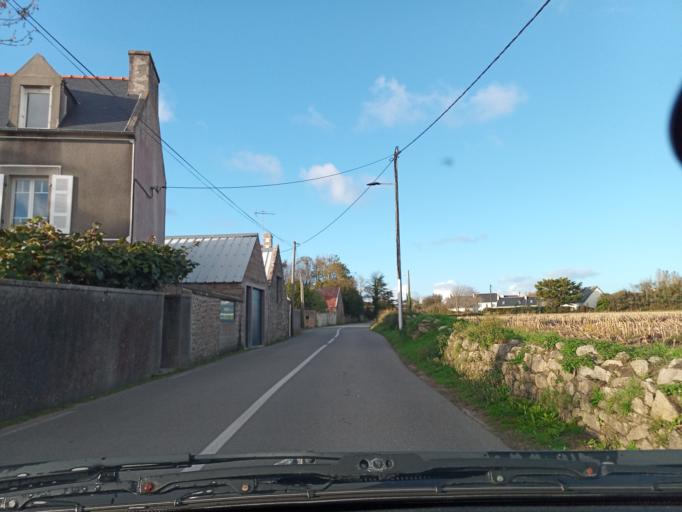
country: FR
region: Brittany
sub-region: Departement du Finistere
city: Esquibien
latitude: 48.0176
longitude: -4.5648
